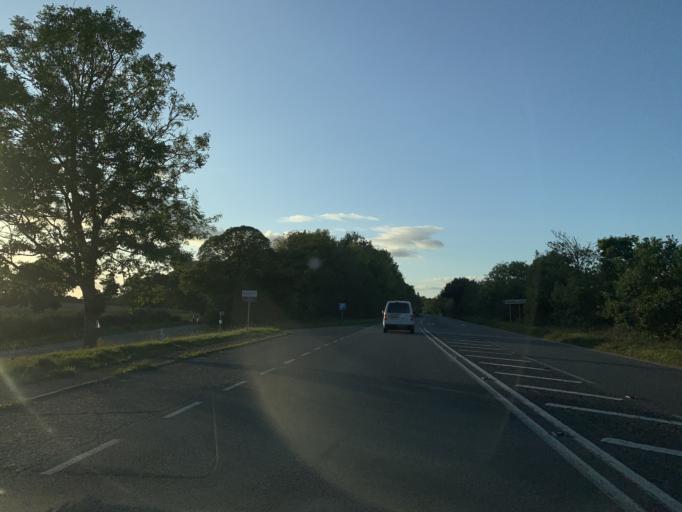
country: GB
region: England
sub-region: Wiltshire
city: Whiteparish
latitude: 50.9768
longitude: -1.6271
